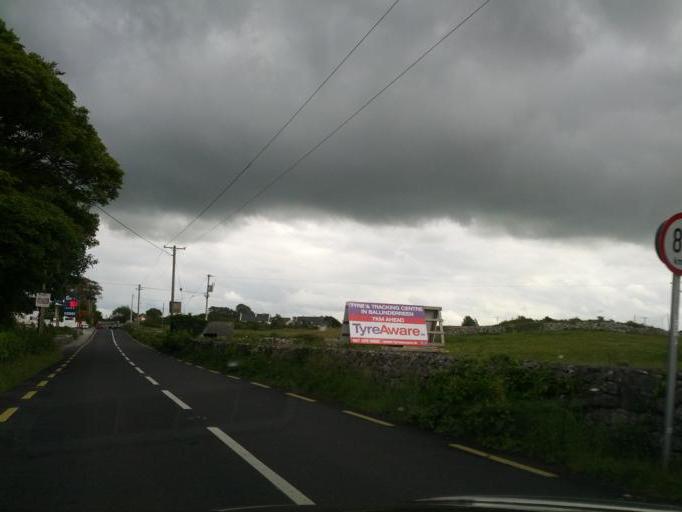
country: IE
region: Connaught
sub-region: County Galway
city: Oranmore
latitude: 53.1397
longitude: -8.9562
